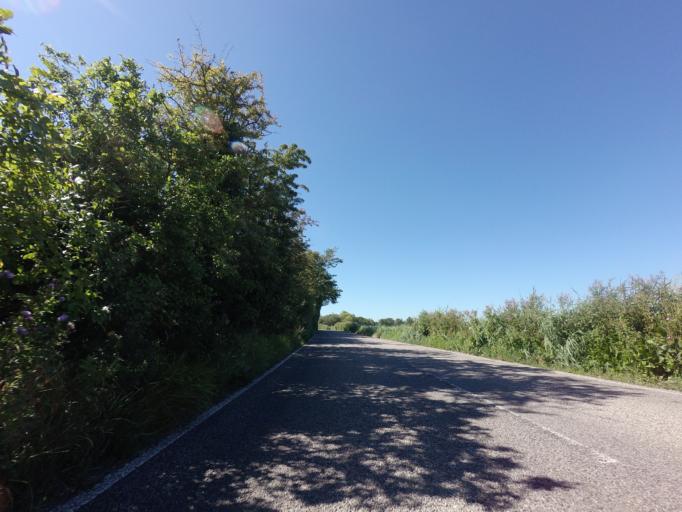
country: GB
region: England
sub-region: Kent
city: Ash
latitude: 51.3165
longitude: 1.2129
